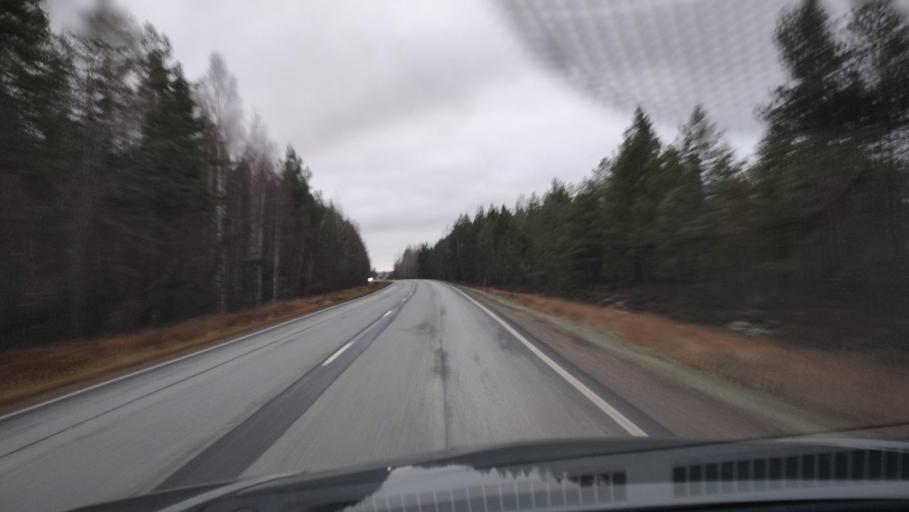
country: FI
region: Southern Ostrobothnia
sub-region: Suupohja
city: Kauhajoki
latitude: 62.3811
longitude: 22.1084
